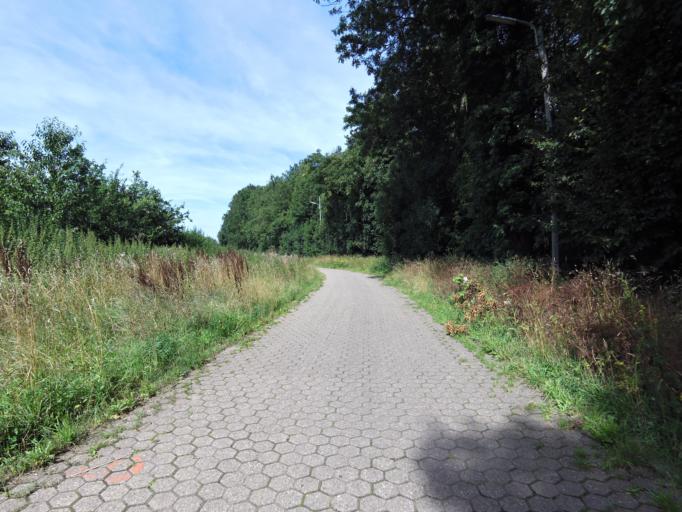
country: DE
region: North Rhine-Westphalia
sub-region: Regierungsbezirk Koln
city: Herzogenrath
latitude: 50.8645
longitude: 6.1130
